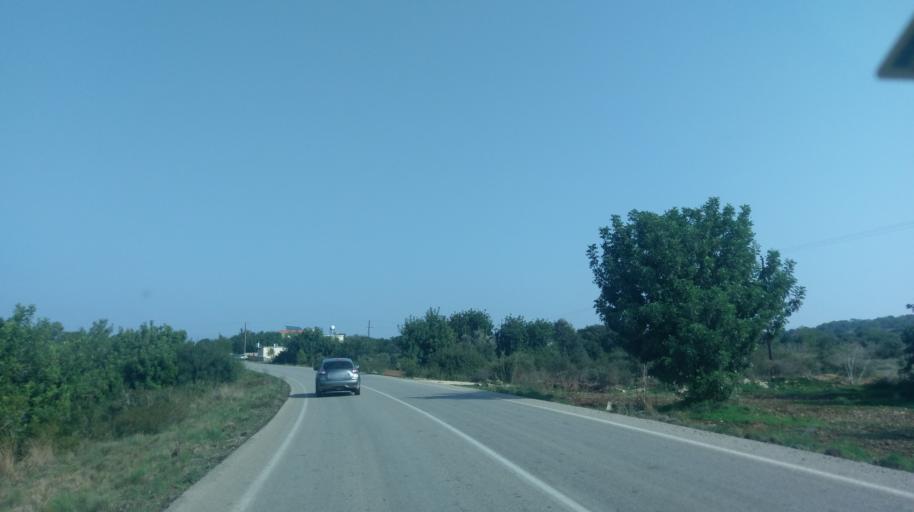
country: CY
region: Ammochostos
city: Leonarisso
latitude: 35.5212
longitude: 34.1735
